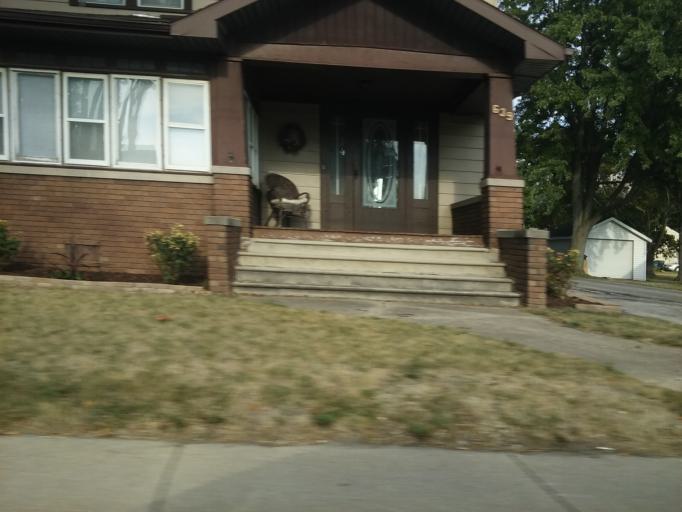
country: US
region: Ohio
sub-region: Wood County
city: Bowling Green
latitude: 41.3656
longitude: -83.6504
